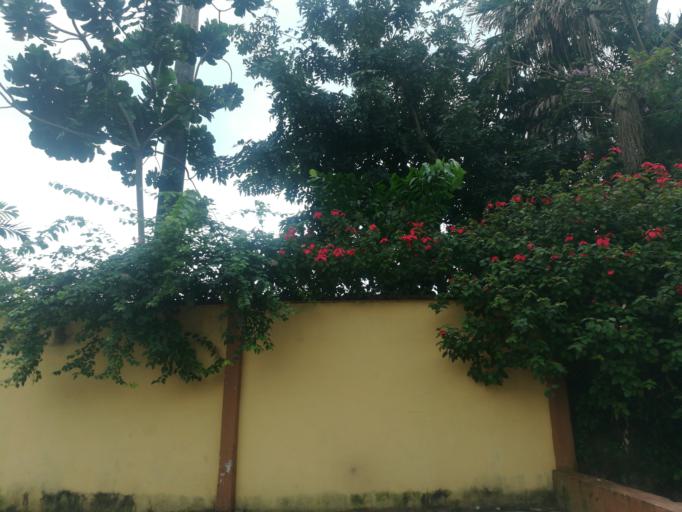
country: NG
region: Lagos
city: Ojota
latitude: 6.5708
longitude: 3.3688
